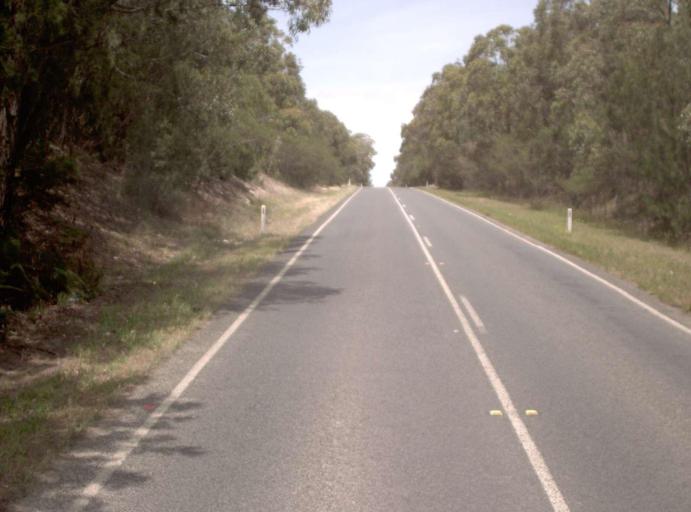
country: AU
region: Victoria
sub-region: Latrobe
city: Traralgon
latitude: -38.5376
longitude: 146.7033
